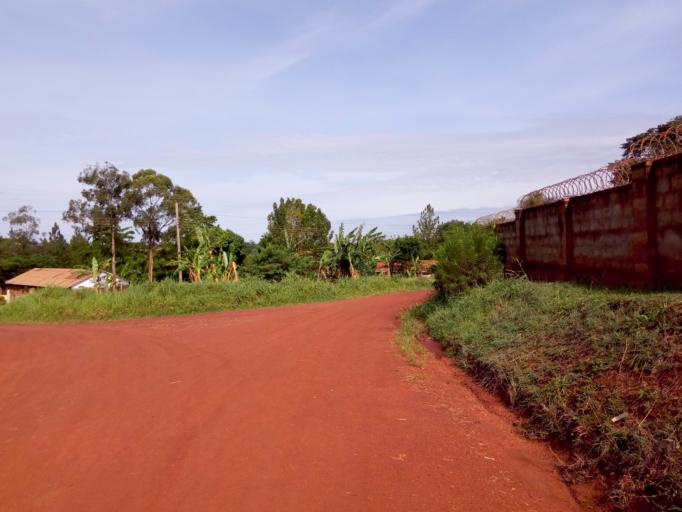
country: UG
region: Western Region
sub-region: Masindi District
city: Masindi
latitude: 1.6863
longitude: 31.7158
